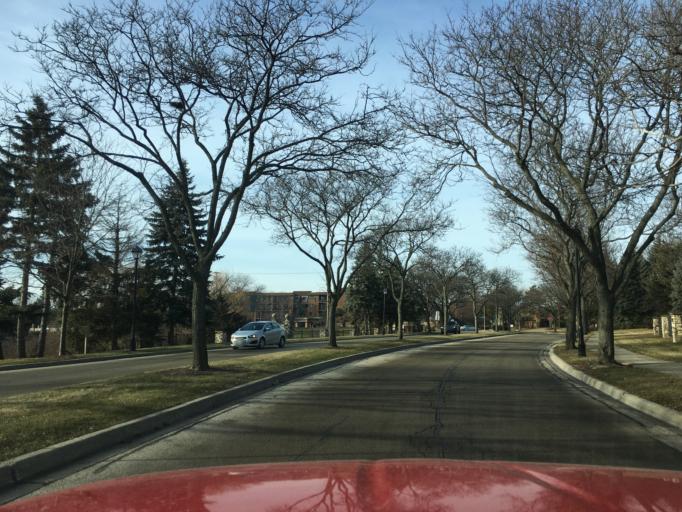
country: US
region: Illinois
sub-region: Cook County
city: Buffalo Grove
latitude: 42.1425
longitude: -87.9568
